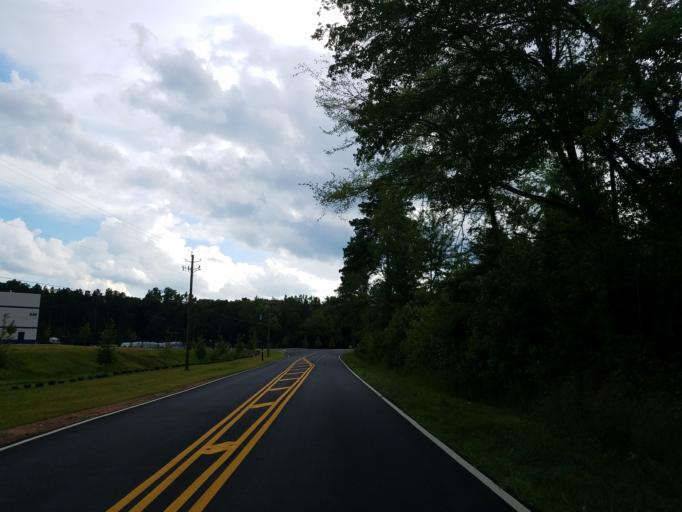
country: US
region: Georgia
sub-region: Bartow County
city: Cartersville
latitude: 34.2682
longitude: -84.8290
